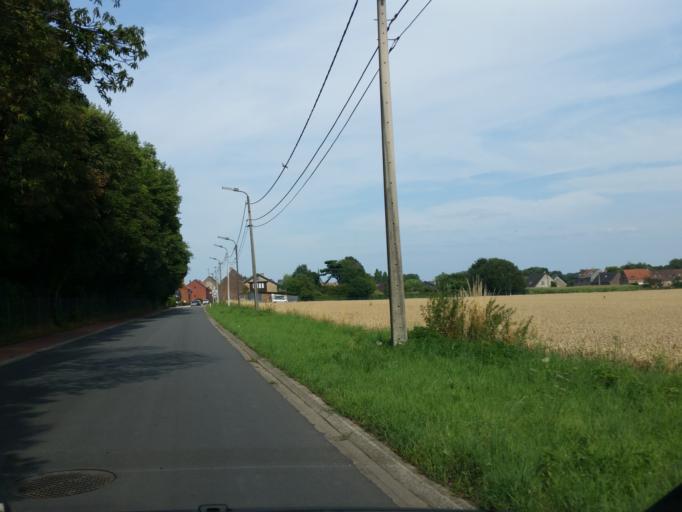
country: BE
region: Flanders
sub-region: Provincie Vlaams-Brabant
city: Zemst
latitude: 50.9592
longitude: 4.4469
